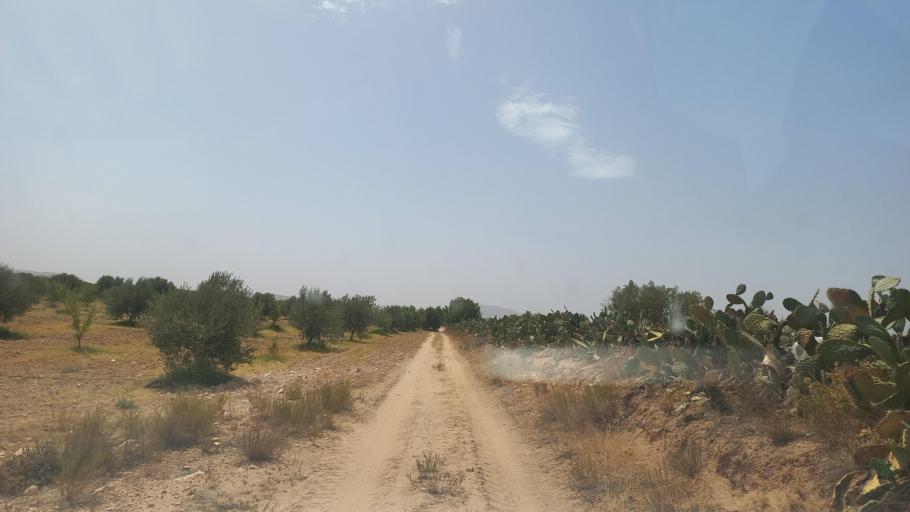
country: TN
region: Al Qasrayn
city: Kasserine
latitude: 35.2620
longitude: 9.0057
